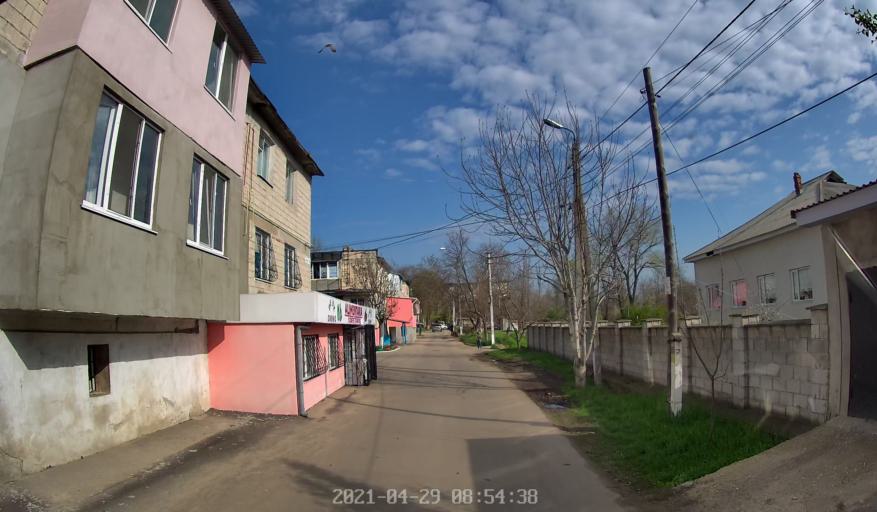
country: MD
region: Chisinau
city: Cricova
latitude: 47.1358
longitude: 28.8604
